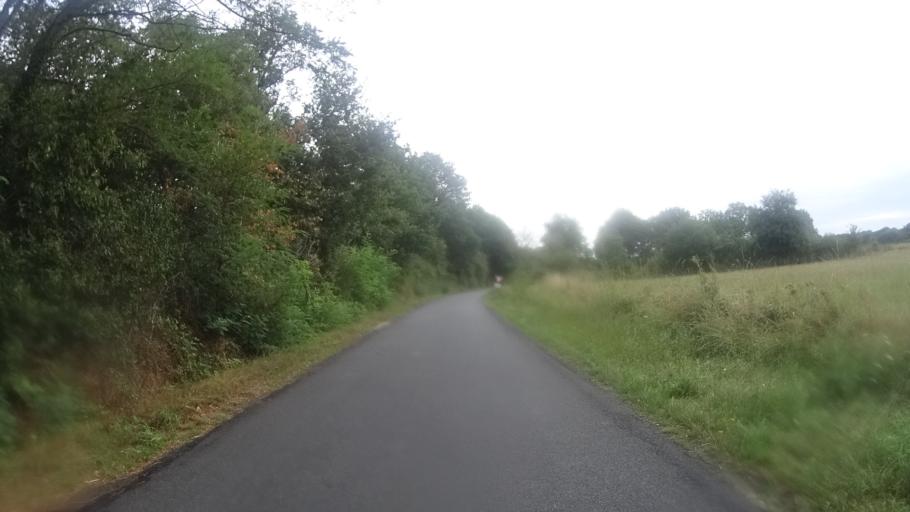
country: FR
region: Centre
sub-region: Departement du Loiret
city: Fay-aux-Loges
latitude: 47.9635
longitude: 2.1822
